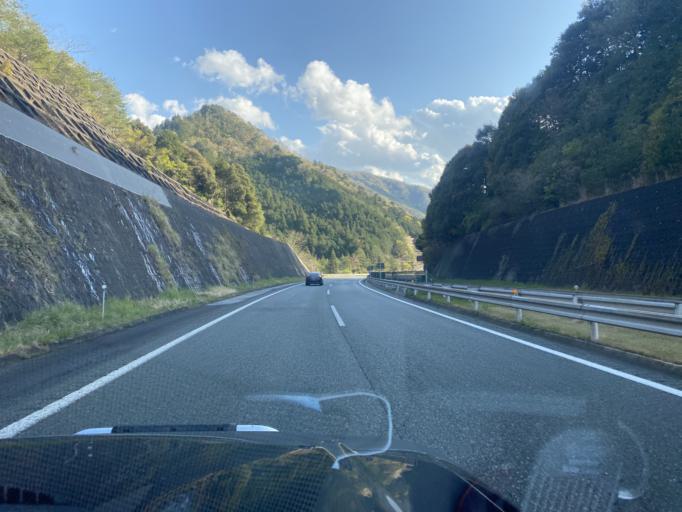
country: JP
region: Hyogo
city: Sasayama
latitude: 35.0214
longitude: 135.1768
